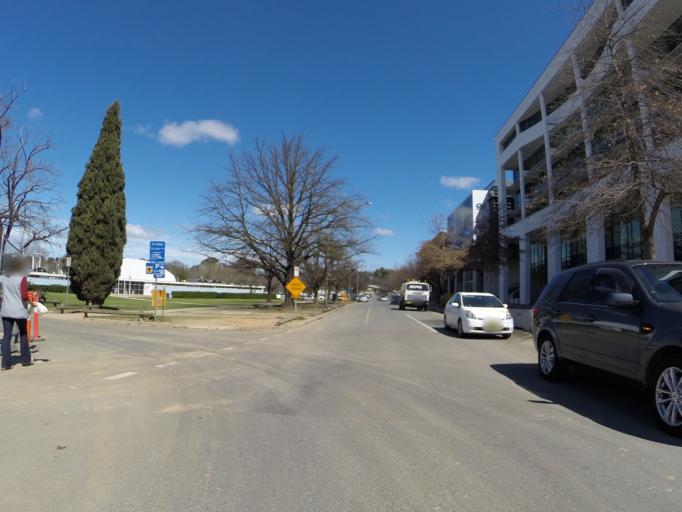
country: AU
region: Australian Capital Territory
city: Canberra
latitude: -35.2842
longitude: 149.1323
